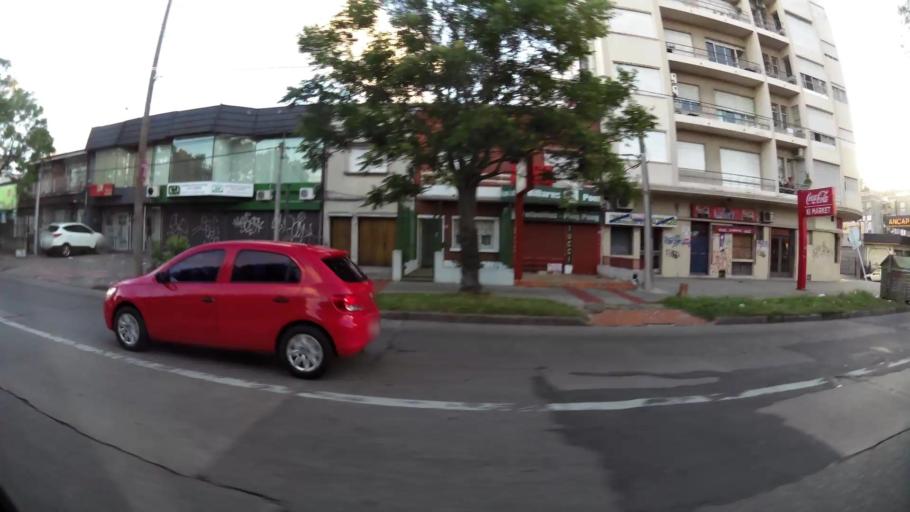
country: UY
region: Montevideo
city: Montevideo
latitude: -34.8868
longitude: -56.1343
